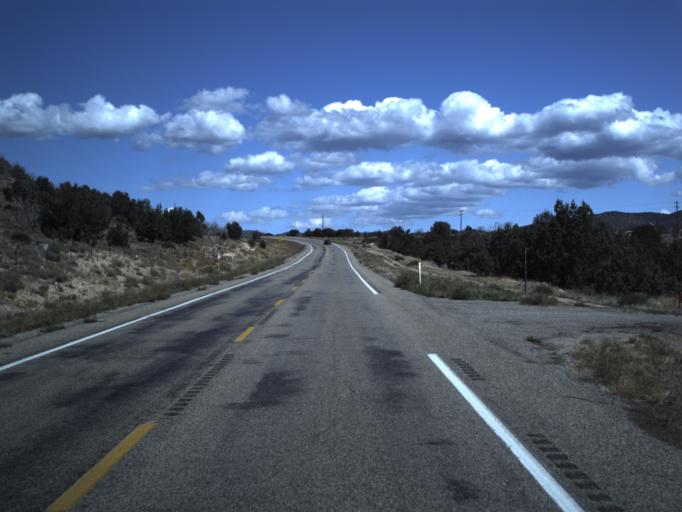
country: US
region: Utah
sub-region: Washington County
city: Ivins
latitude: 37.3723
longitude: -113.6604
